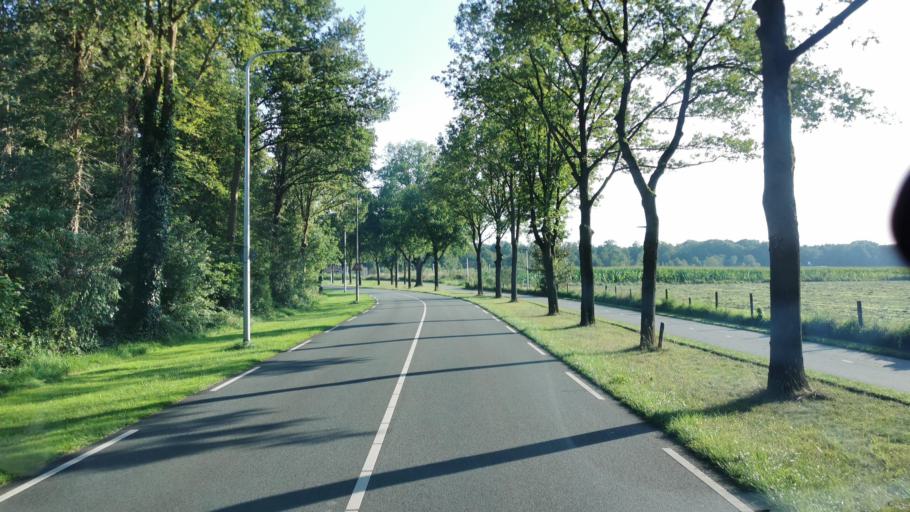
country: NL
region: Overijssel
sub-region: Gemeente Oldenzaal
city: Oldenzaal
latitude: 52.3151
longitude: 6.8942
